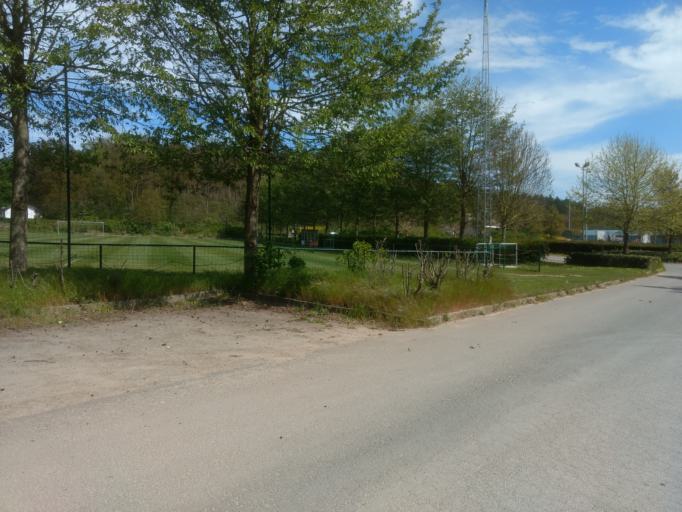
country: BE
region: Flanders
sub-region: Provincie Vlaams-Brabant
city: Oud-Heverlee
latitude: 50.8276
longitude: 4.6577
